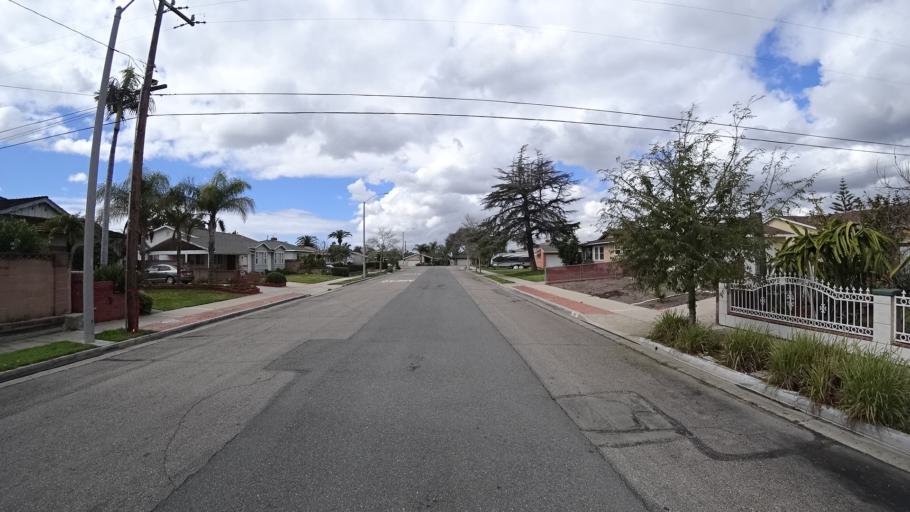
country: US
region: California
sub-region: Orange County
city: Anaheim
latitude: 33.8231
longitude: -117.9312
